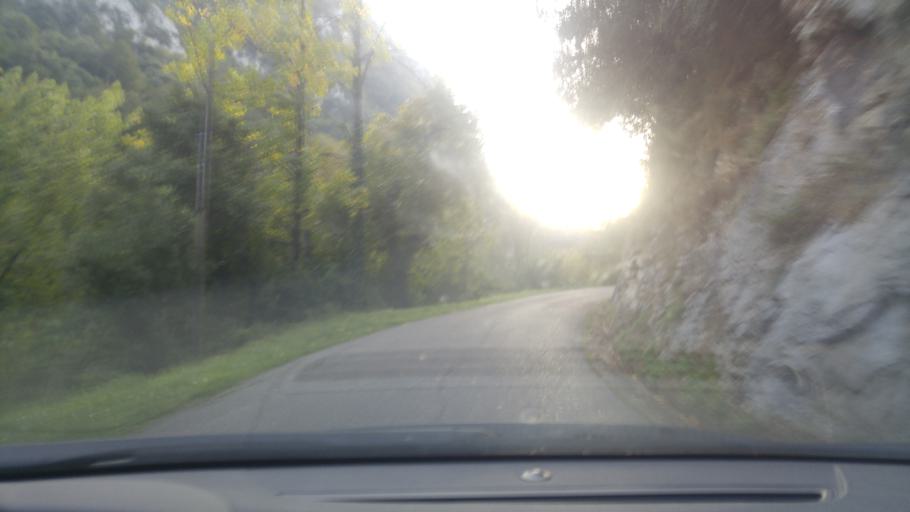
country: ES
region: Asturias
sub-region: Province of Asturias
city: Proaza
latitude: 43.2479
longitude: -6.0267
